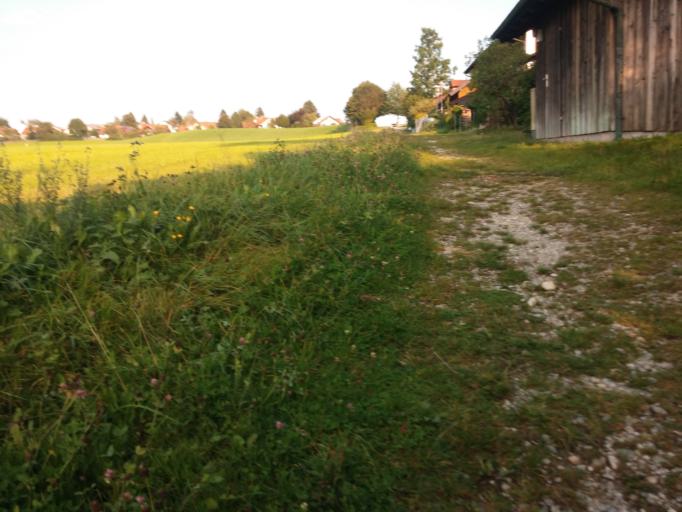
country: DE
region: Bavaria
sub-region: Upper Bavaria
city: Oberpframmern
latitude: 48.0188
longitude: 11.8050
